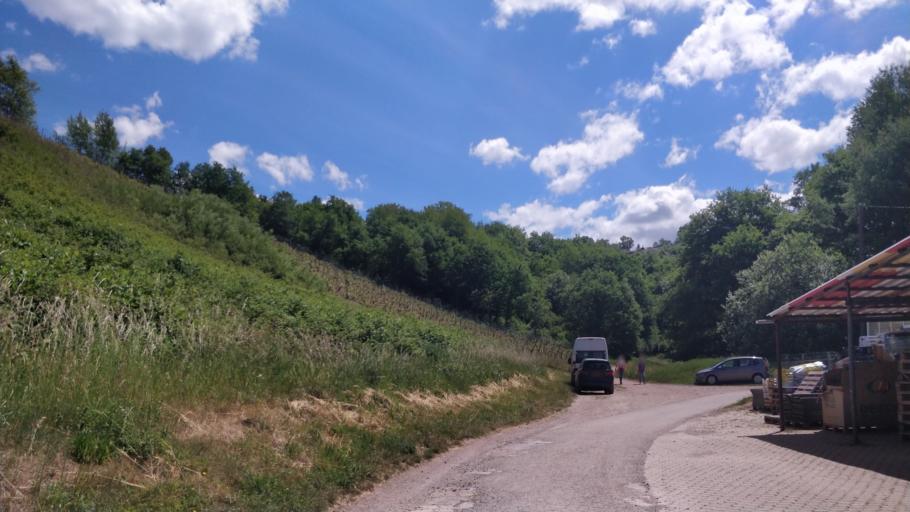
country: DE
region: Rheinland-Pfalz
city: Irsch
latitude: 49.7379
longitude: 6.6679
